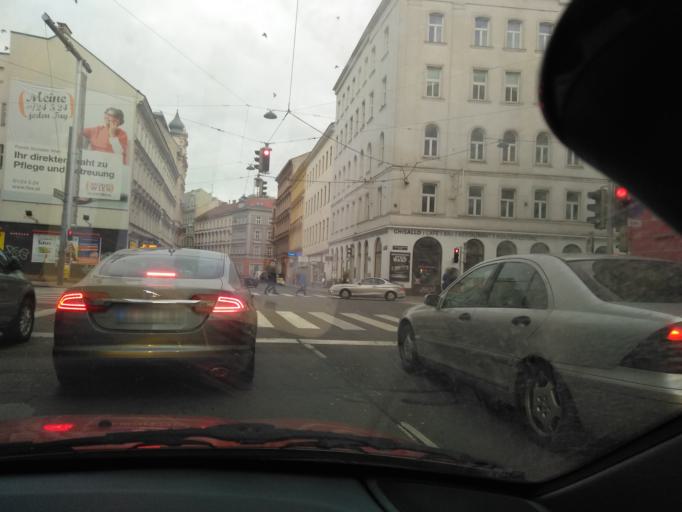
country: AT
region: Vienna
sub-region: Wien Stadt
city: Vienna
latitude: 48.1893
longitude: 16.3514
